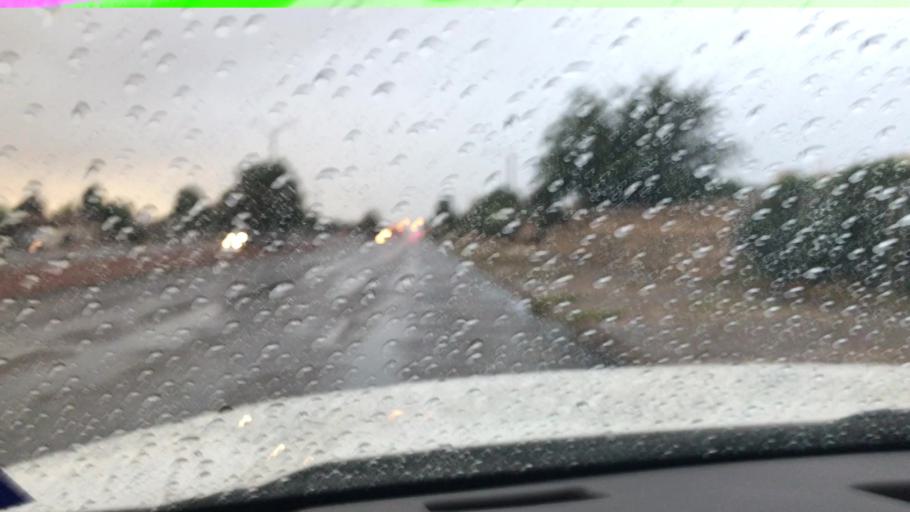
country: US
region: Texas
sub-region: El Paso County
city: Fort Bliss
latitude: 31.7951
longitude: -106.3234
